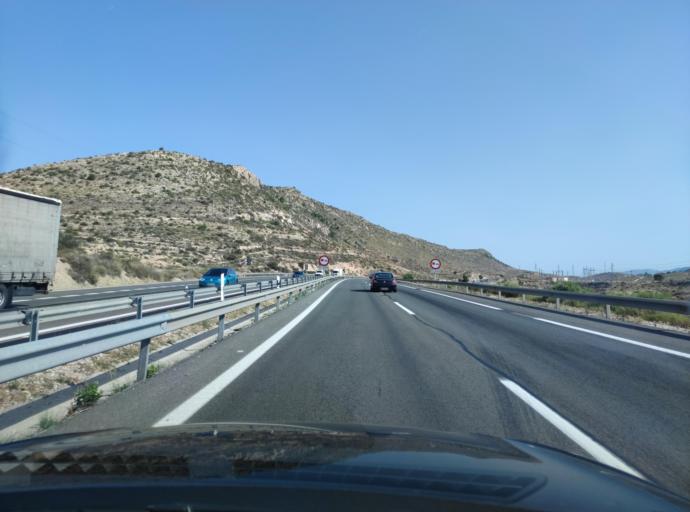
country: ES
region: Valencia
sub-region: Provincia de Alicante
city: Elda
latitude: 38.4329
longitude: -0.7826
